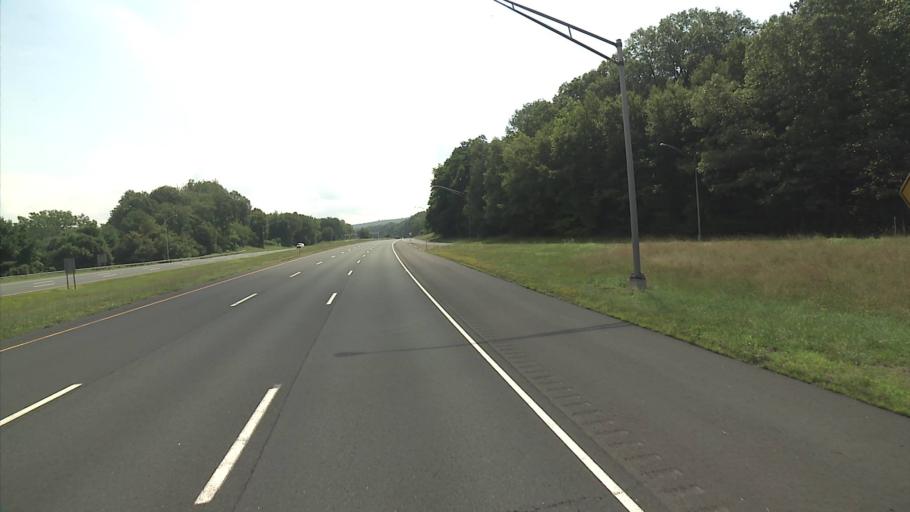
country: US
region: Connecticut
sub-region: Hartford County
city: Manchester
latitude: 41.7622
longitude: -72.5176
